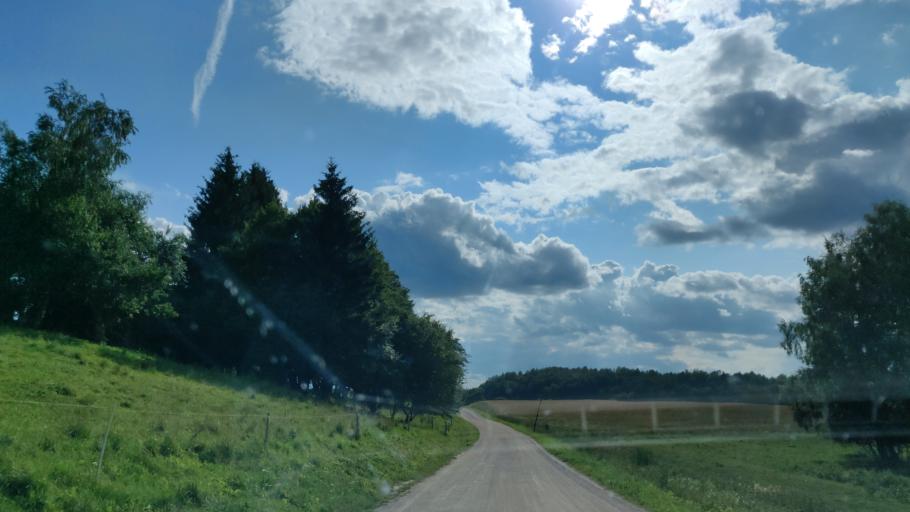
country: LT
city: Varniai
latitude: 55.6084
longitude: 22.3274
